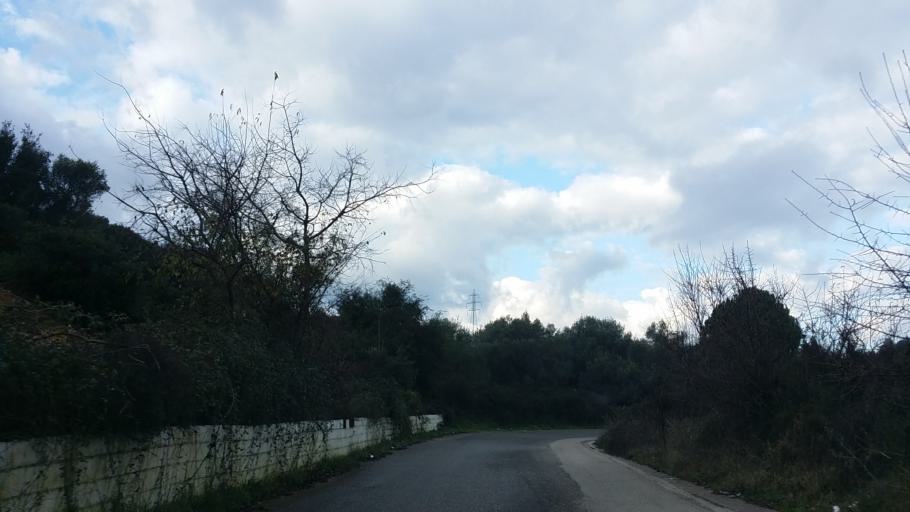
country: GR
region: West Greece
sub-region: Nomos Aitolias kai Akarnanias
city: Katouna
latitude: 38.7802
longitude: 21.1171
